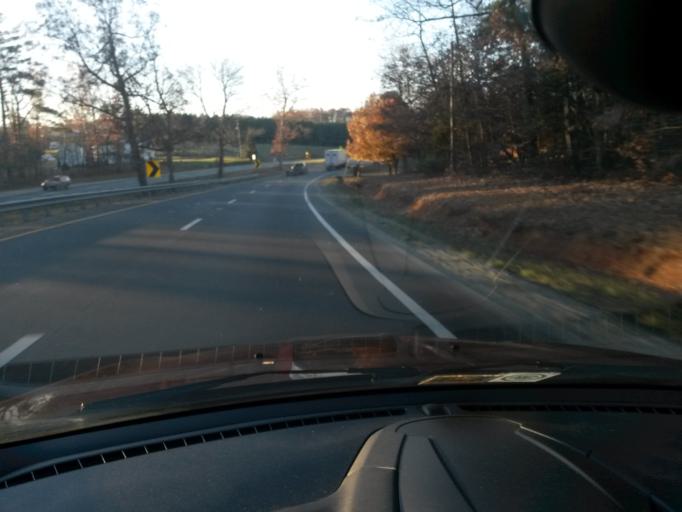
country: US
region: Virginia
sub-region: Franklin County
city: Henry Fork
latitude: 36.8872
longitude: -79.8654
